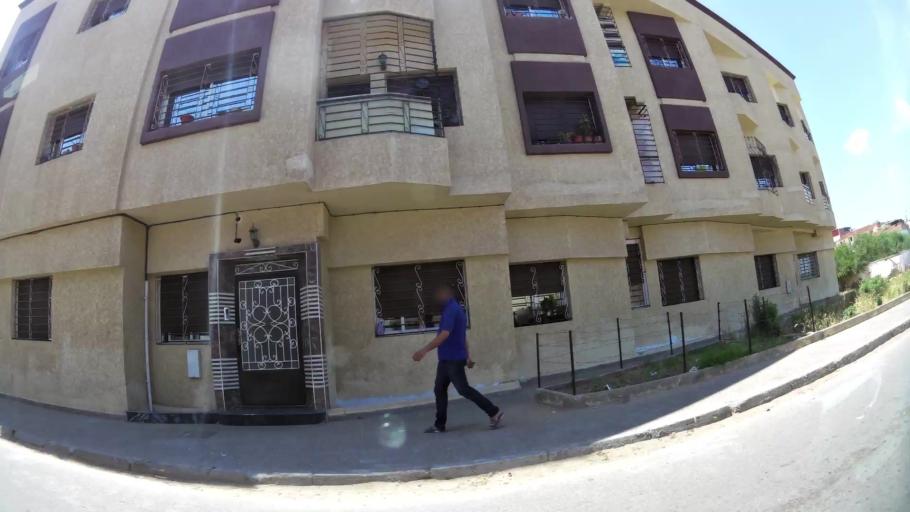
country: MA
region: Gharb-Chrarda-Beni Hssen
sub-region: Kenitra Province
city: Kenitra
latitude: 34.2605
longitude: -6.5564
